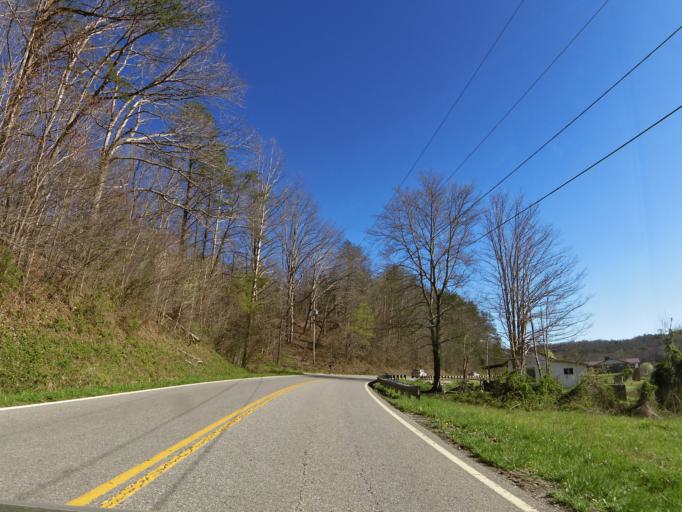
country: US
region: Tennessee
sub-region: Scott County
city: Huntsville
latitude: 36.4557
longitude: -84.4745
